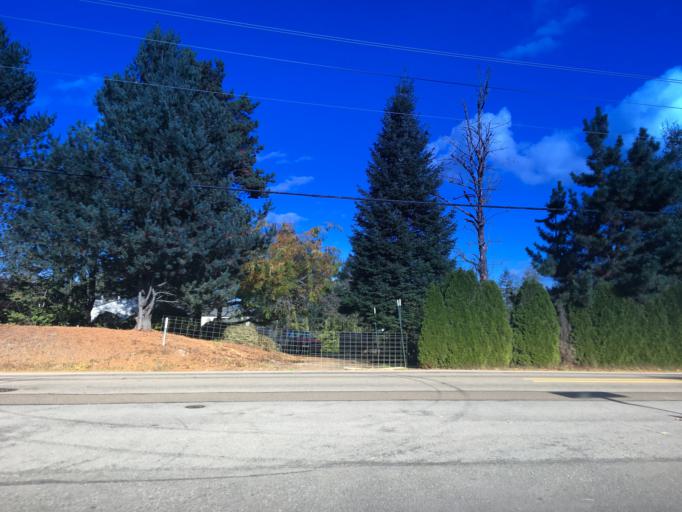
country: US
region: Oregon
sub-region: Multnomah County
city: Troutdale
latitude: 45.5027
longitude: -122.3890
